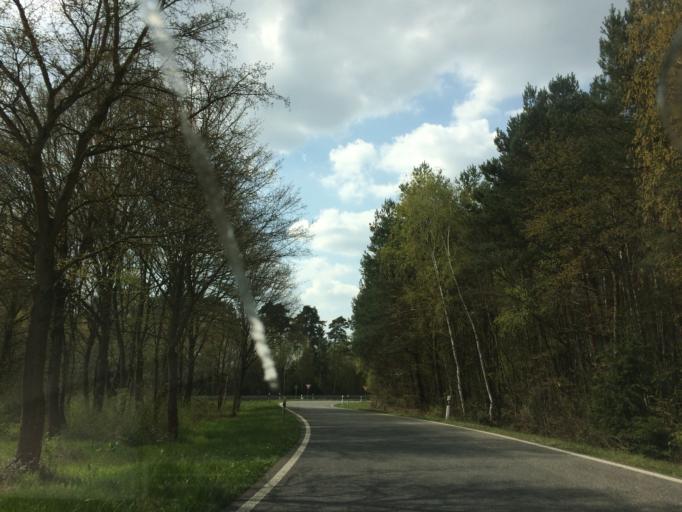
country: DE
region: Hesse
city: Obertshausen
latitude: 50.0850
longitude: 8.8450
